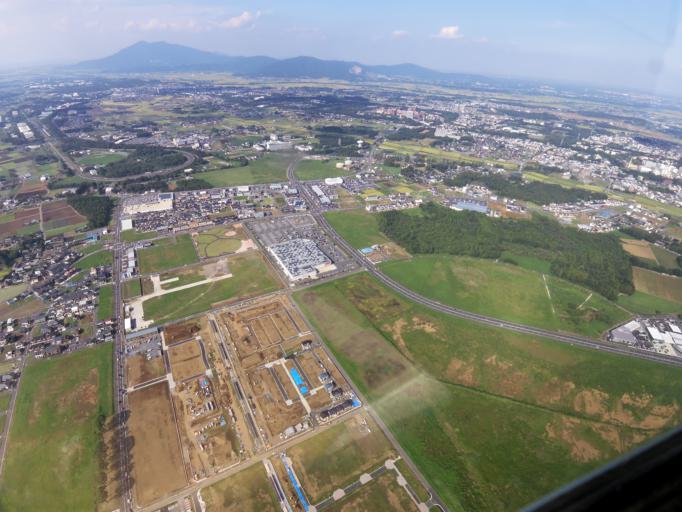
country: JP
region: Ibaraki
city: Naka
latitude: 36.0905
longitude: 140.0762
